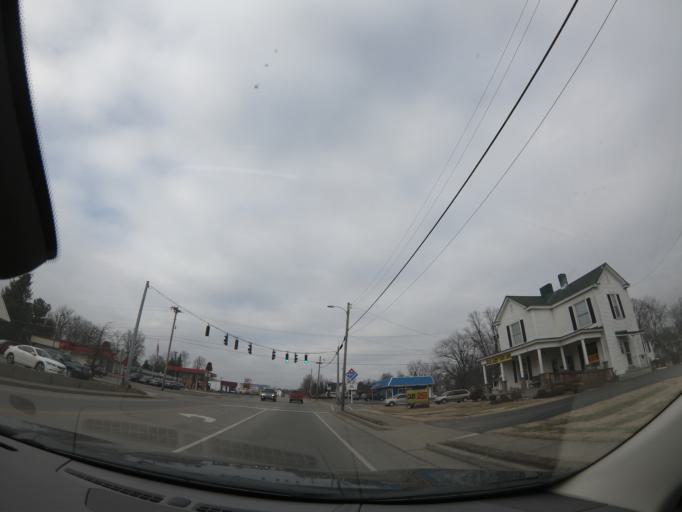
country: US
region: Kentucky
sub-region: Nelson County
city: Bardstown
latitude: 37.8192
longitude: -85.4635
